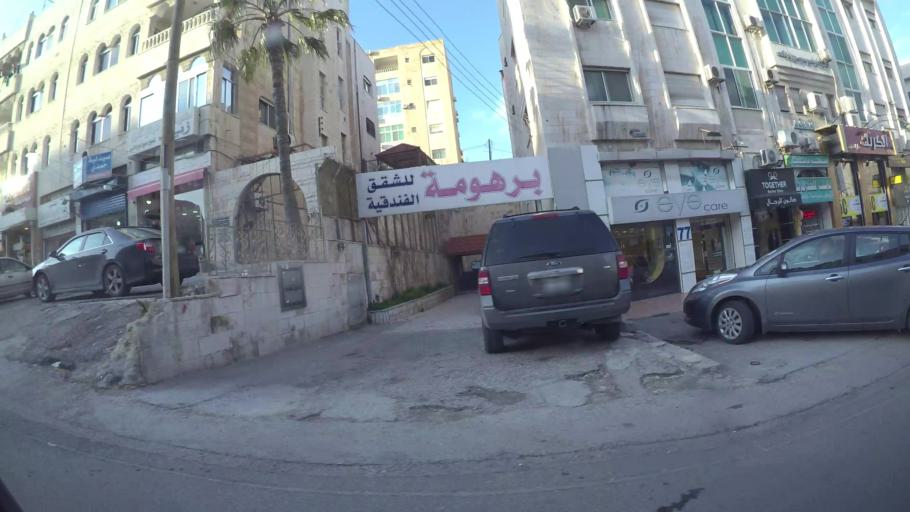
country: JO
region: Amman
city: Al Jubayhah
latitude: 31.9991
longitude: 35.8703
